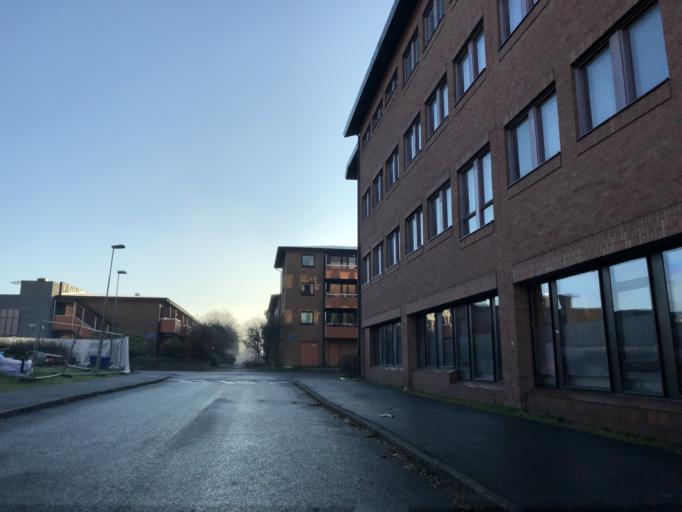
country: SE
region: Vaestra Goetaland
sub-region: Goteborg
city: Rannebergen
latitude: 57.7978
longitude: 12.0525
